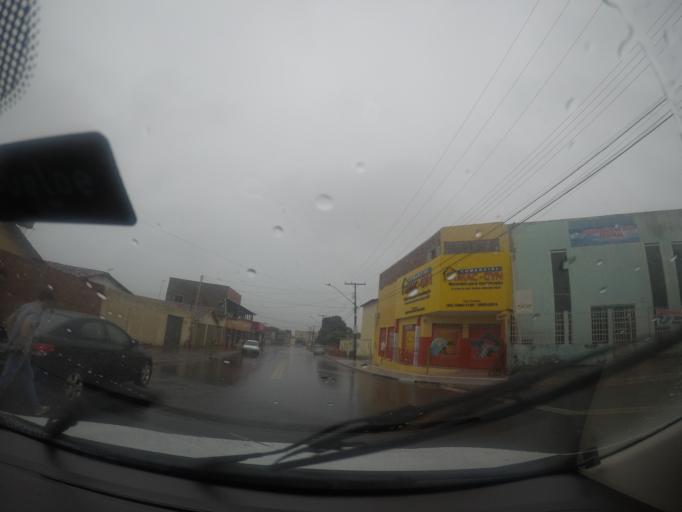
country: BR
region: Goias
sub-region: Goiania
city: Goiania
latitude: -16.5969
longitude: -49.3300
